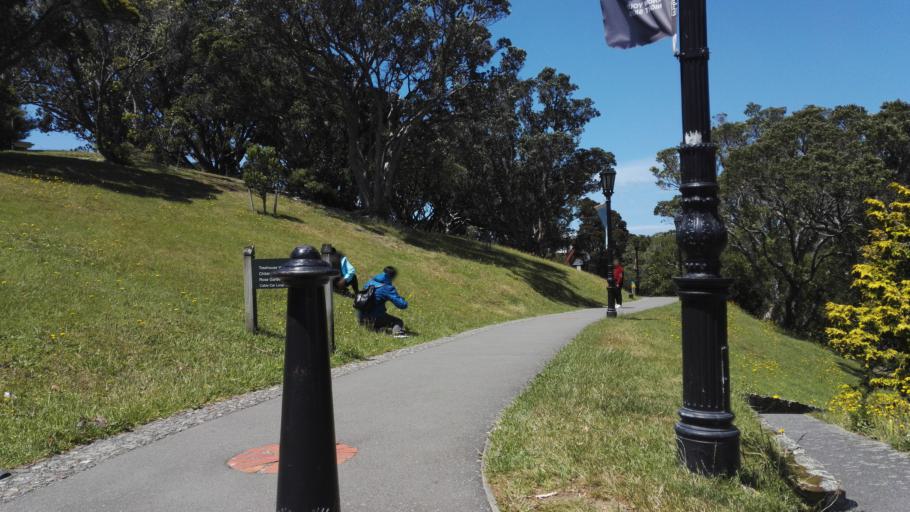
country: NZ
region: Wellington
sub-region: Wellington City
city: Kelburn
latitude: -41.2844
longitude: 174.7674
